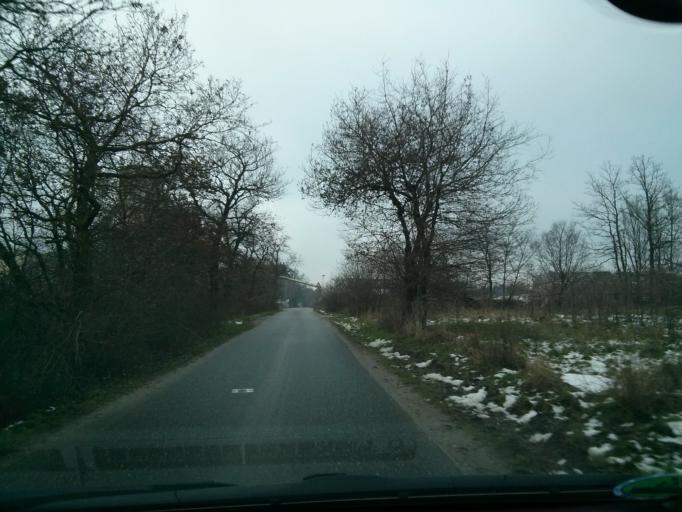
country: DE
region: North Rhine-Westphalia
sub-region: Regierungsbezirk Koln
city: Alfter
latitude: 50.6789
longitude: 7.0040
